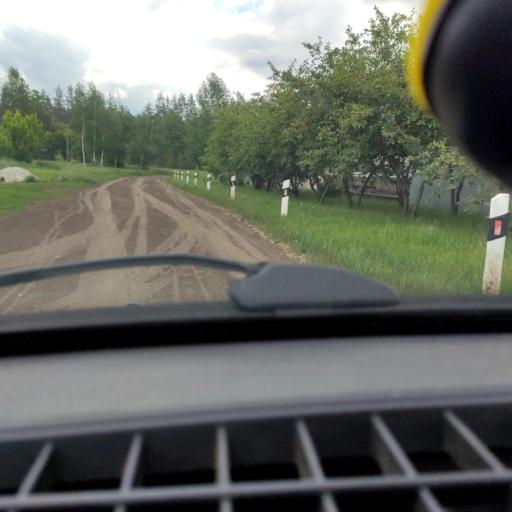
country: RU
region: Samara
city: Povolzhskiy
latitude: 53.5949
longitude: 49.5829
